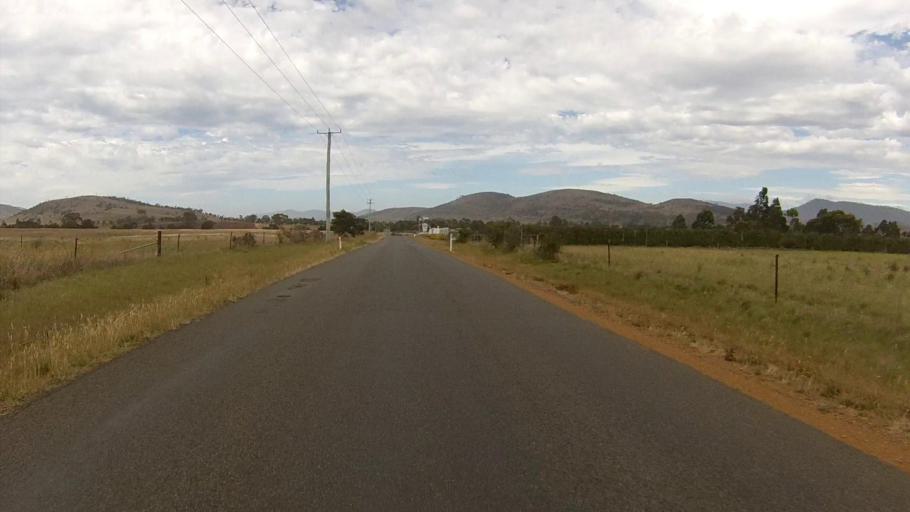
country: AU
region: Tasmania
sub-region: Clarence
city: Cambridge
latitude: -42.7253
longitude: 147.4499
